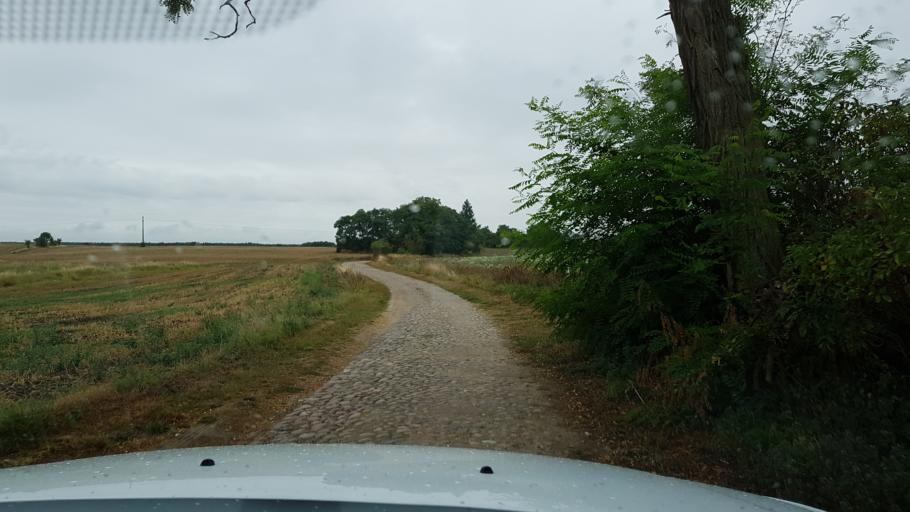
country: PL
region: West Pomeranian Voivodeship
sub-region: Powiat gryfinski
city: Cedynia
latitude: 52.8503
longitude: 14.2898
